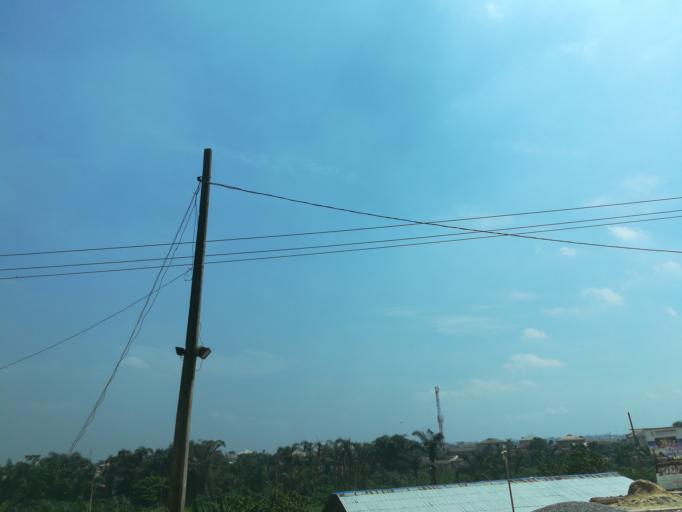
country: NG
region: Lagos
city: Ikorodu
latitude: 6.6608
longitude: 3.4712
